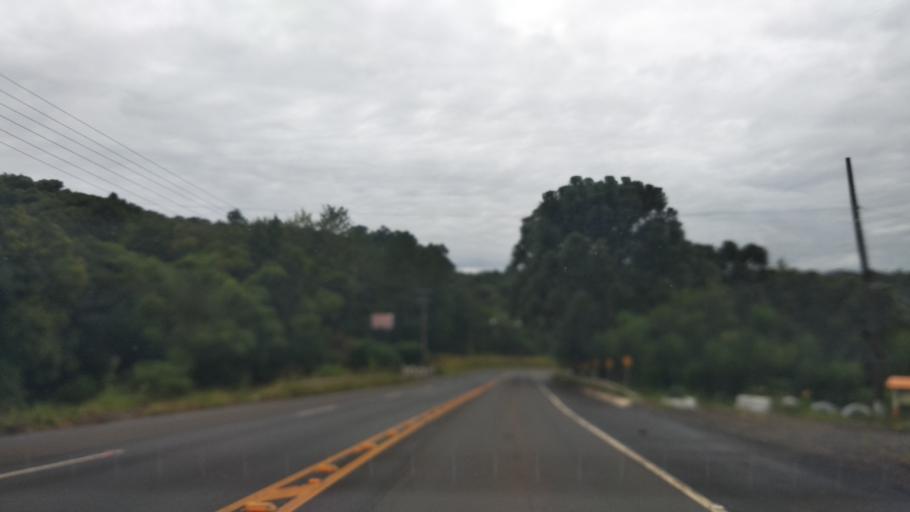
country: BR
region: Santa Catarina
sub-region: Videira
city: Videira
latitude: -27.0436
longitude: -51.1546
